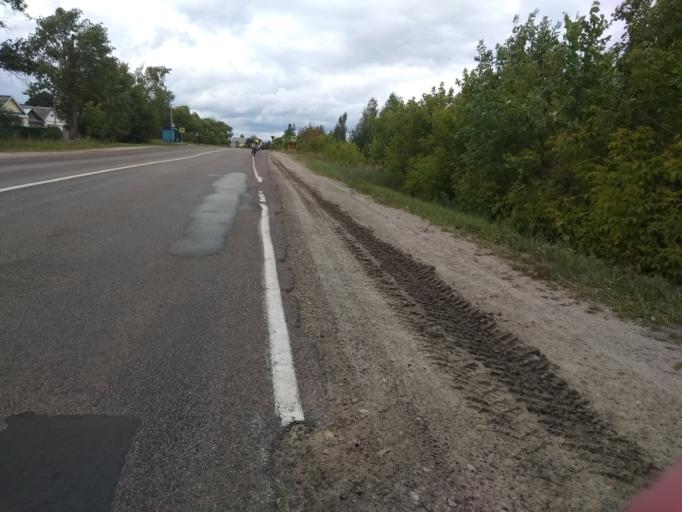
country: RU
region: Moskovskaya
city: Kerva
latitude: 55.5893
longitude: 39.7011
